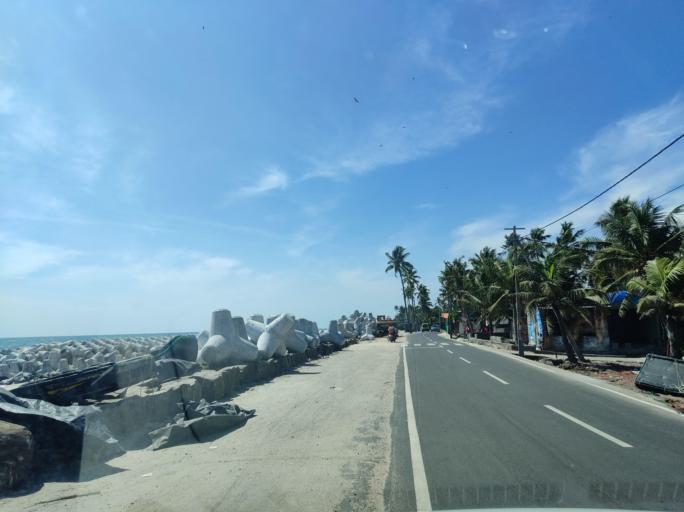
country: IN
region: Kerala
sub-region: Alappuzha
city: Kayankulam
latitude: 9.2141
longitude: 76.4278
